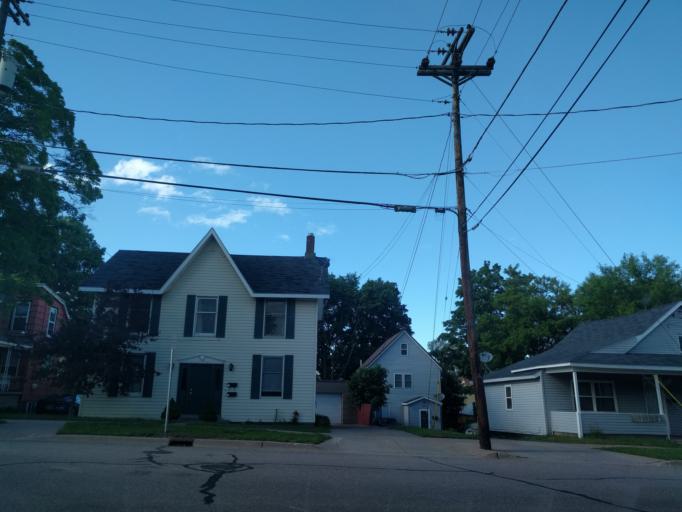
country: US
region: Michigan
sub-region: Marquette County
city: Marquette
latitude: 46.5390
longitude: -87.3957
